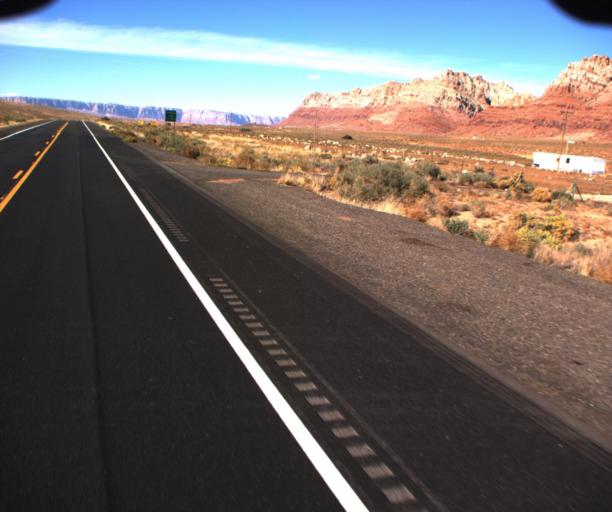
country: US
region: Arizona
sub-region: Coconino County
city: LeChee
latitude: 36.5473
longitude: -111.6231
